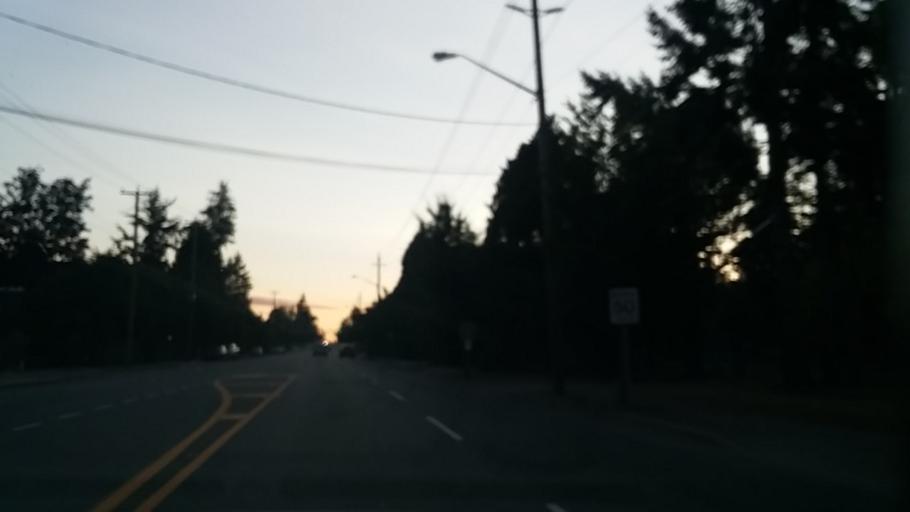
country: CA
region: British Columbia
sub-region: Greater Vancouver Regional District
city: White Rock
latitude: 49.0311
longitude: -122.7801
